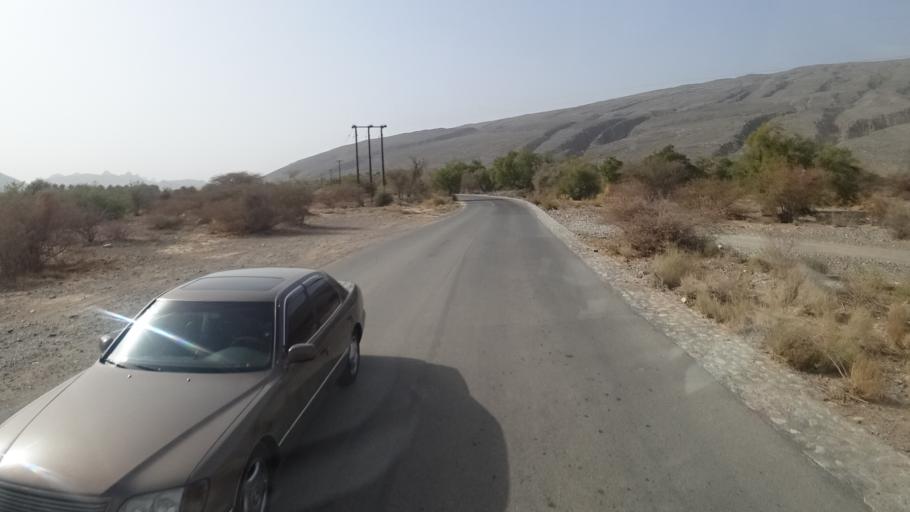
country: OM
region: Muhafazat ad Dakhiliyah
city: Bahla'
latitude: 23.0561
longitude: 57.4120
